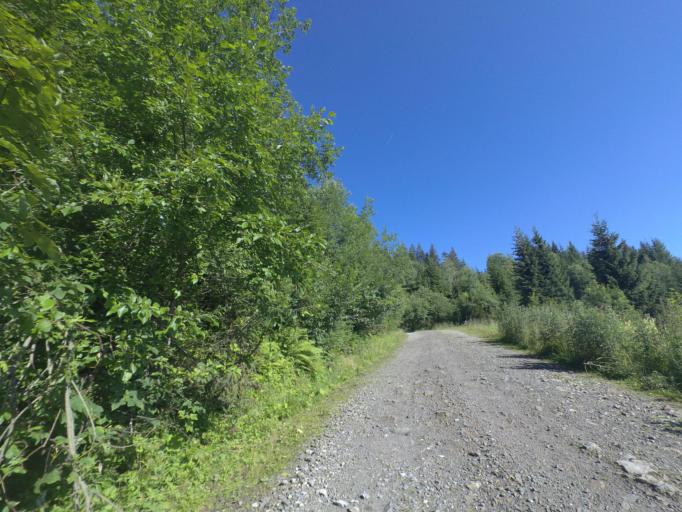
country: AT
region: Salzburg
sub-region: Politischer Bezirk Sankt Johann im Pongau
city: Sankt Veit im Pongau
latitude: 47.3468
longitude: 13.1484
